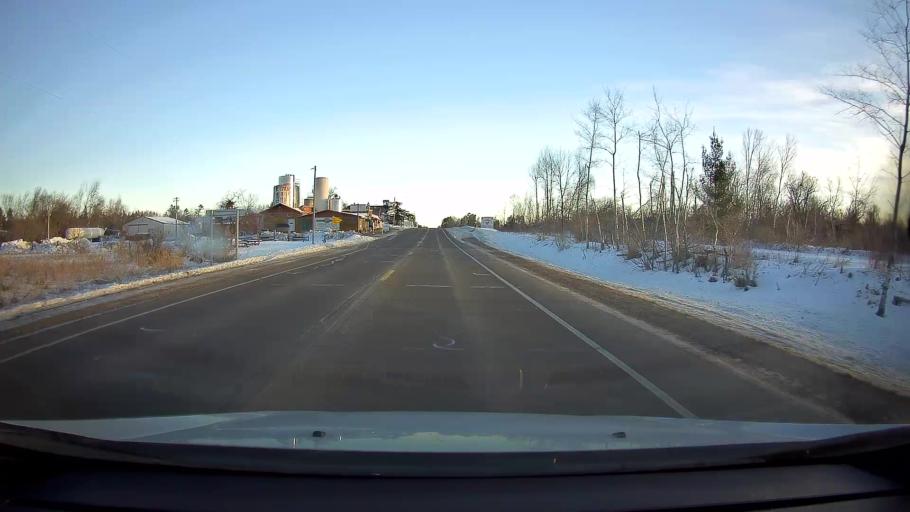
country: US
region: Wisconsin
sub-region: Barron County
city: Cumberland
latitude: 45.4751
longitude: -92.0785
